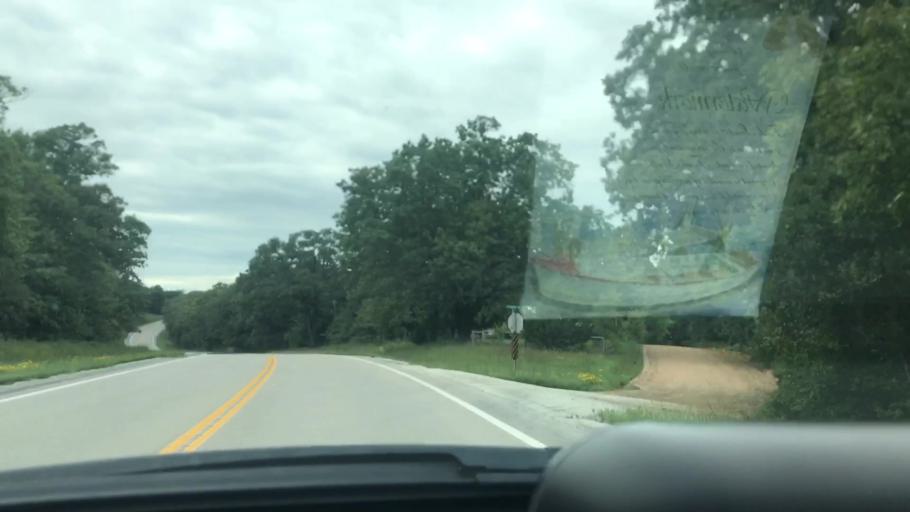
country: US
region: Missouri
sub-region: Benton County
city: Warsaw
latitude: 38.1616
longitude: -93.2997
